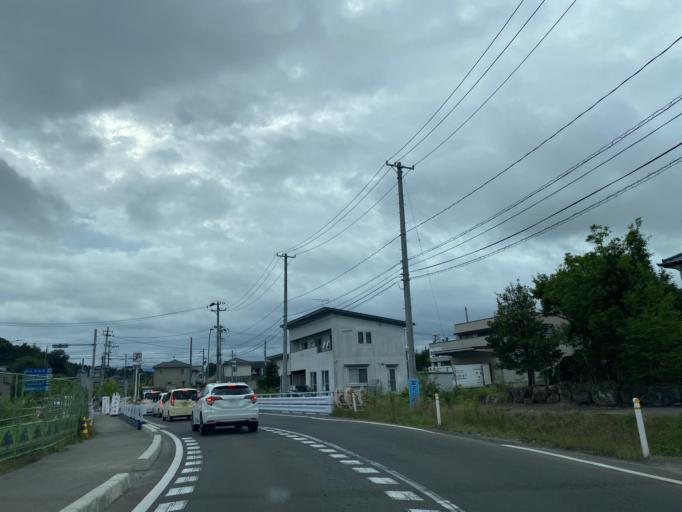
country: JP
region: Miyagi
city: Tomiya
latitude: 38.3954
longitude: 140.8980
